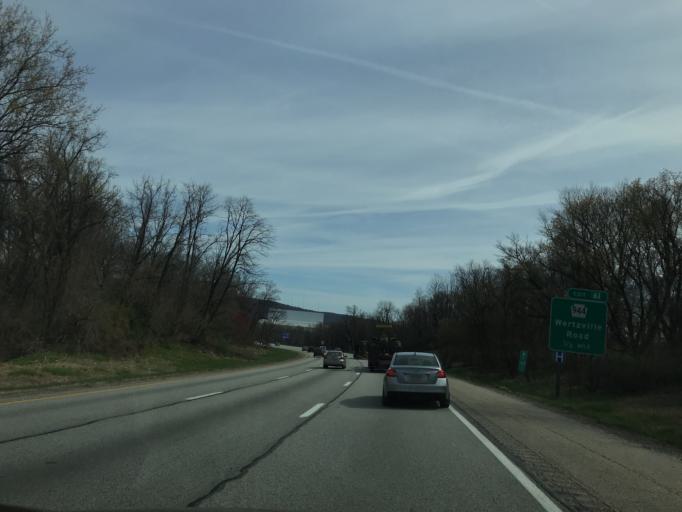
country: US
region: Pennsylvania
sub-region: Cumberland County
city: Enola
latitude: 40.2772
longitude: -76.9851
